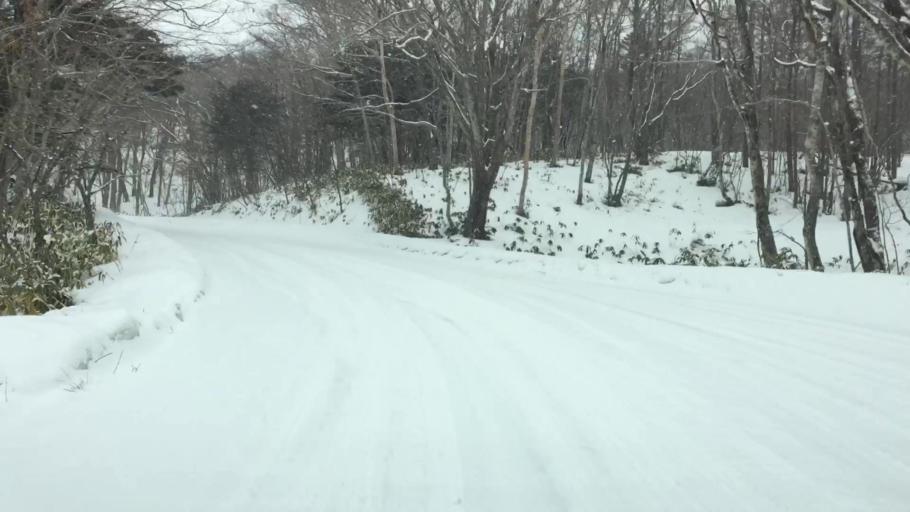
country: JP
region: Tochigi
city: Nikko
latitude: 36.9122
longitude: 139.7382
